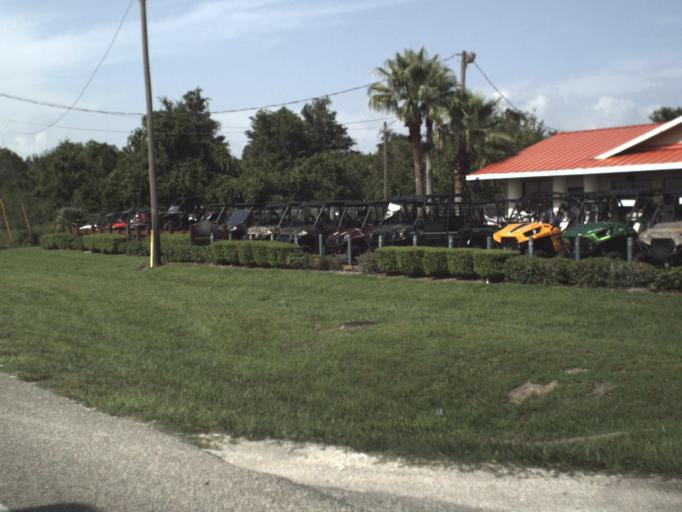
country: US
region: Florida
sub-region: Polk County
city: Lake Wales
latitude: 27.9167
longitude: -81.6040
